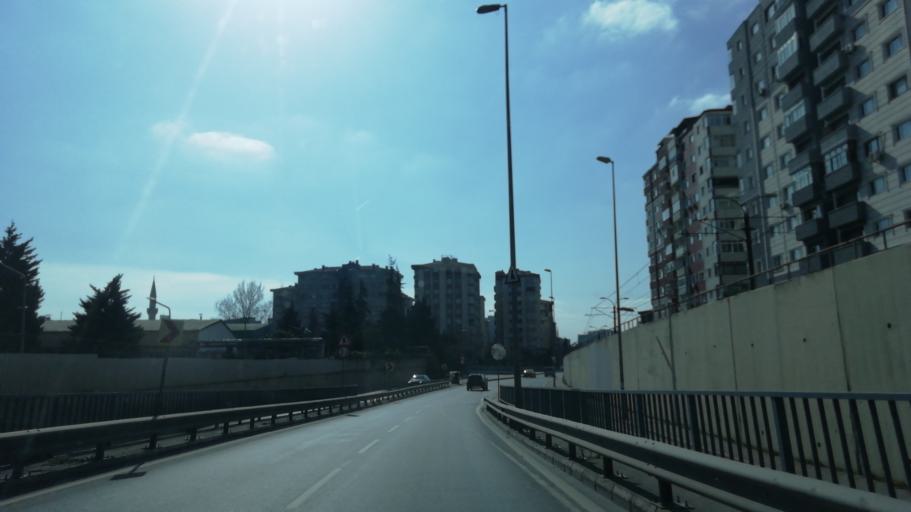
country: TR
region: Istanbul
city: merter keresteciler
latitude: 41.0188
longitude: 28.9009
